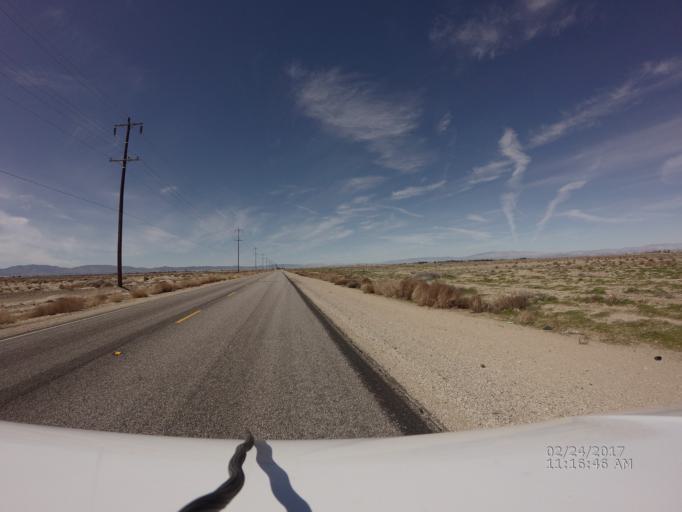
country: US
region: California
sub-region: Los Angeles County
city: Lancaster
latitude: 34.6900
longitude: -118.0340
